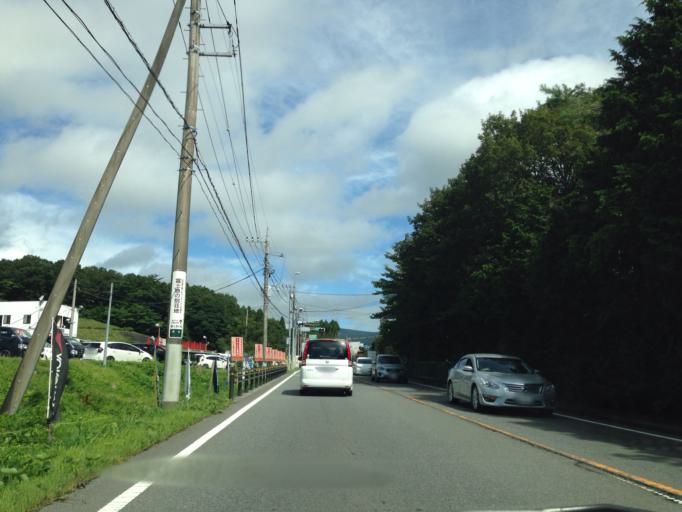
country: JP
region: Shizuoka
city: Gotemba
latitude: 35.3472
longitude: 138.8792
